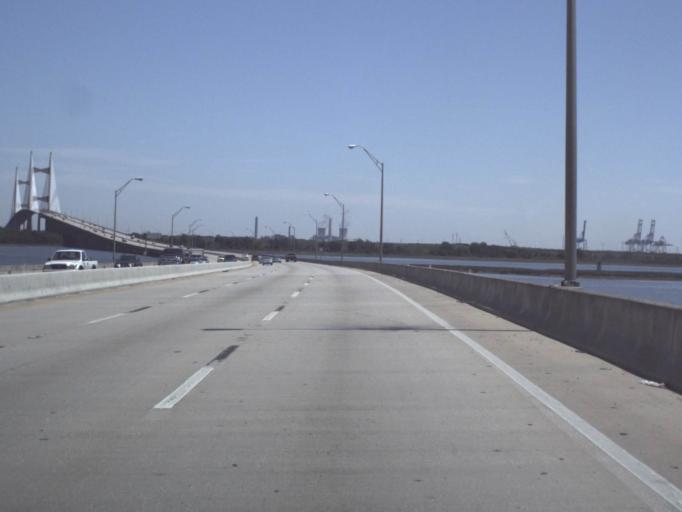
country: US
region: Florida
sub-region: Duval County
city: Jacksonville
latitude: 30.3687
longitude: -81.5515
